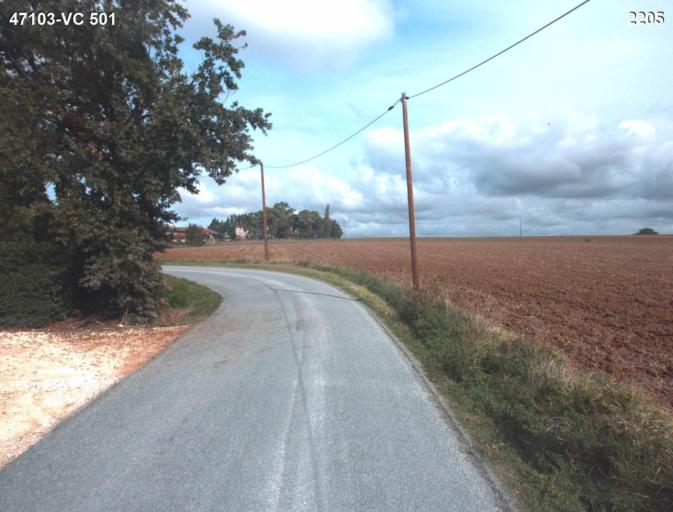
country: FR
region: Aquitaine
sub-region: Departement du Lot-et-Garonne
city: Nerac
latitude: 44.0975
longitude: 0.3279
